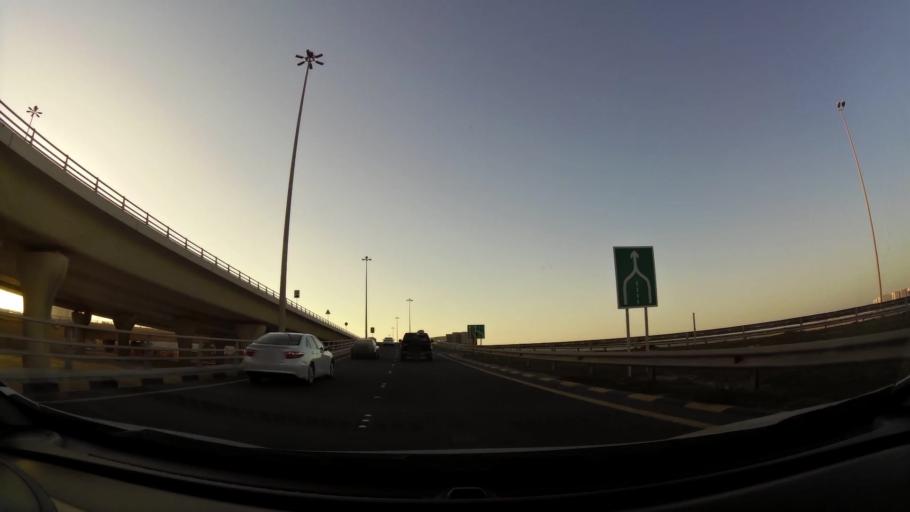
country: BH
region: Muharraq
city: Al Muharraq
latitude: 26.2473
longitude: 50.5895
